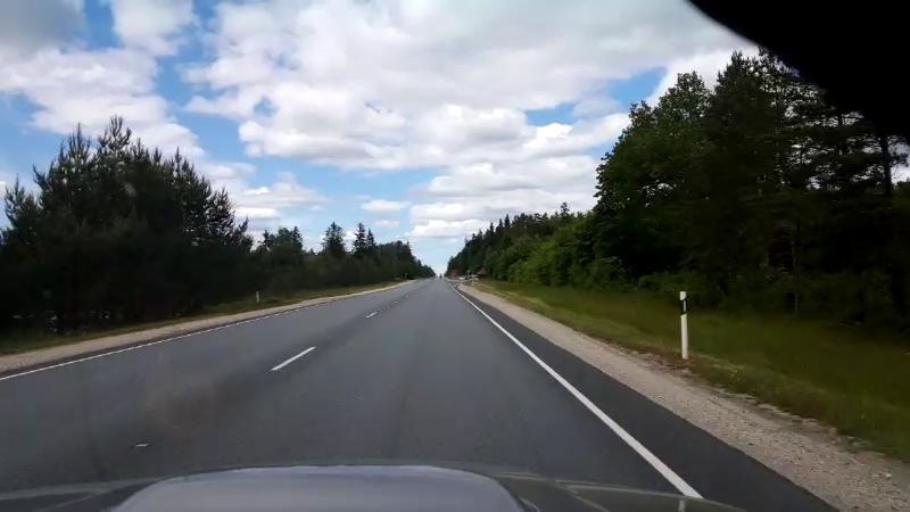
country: EE
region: Raplamaa
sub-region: Maerjamaa vald
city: Marjamaa
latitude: 58.9916
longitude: 24.4665
